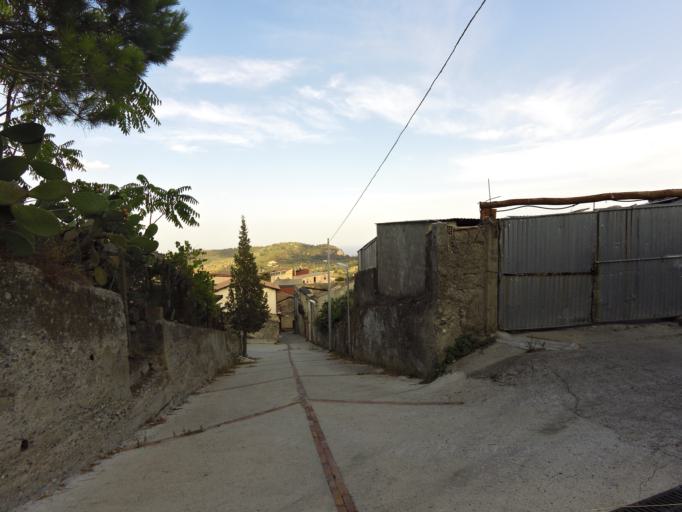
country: IT
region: Calabria
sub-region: Provincia di Reggio Calabria
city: Camini
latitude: 38.4329
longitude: 16.4804
